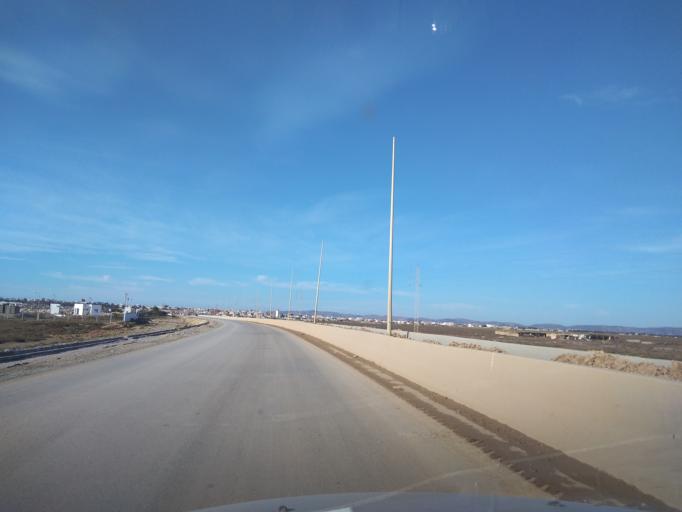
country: TN
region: Ariana
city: Qal'at al Andalus
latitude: 37.0389
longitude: 10.1321
